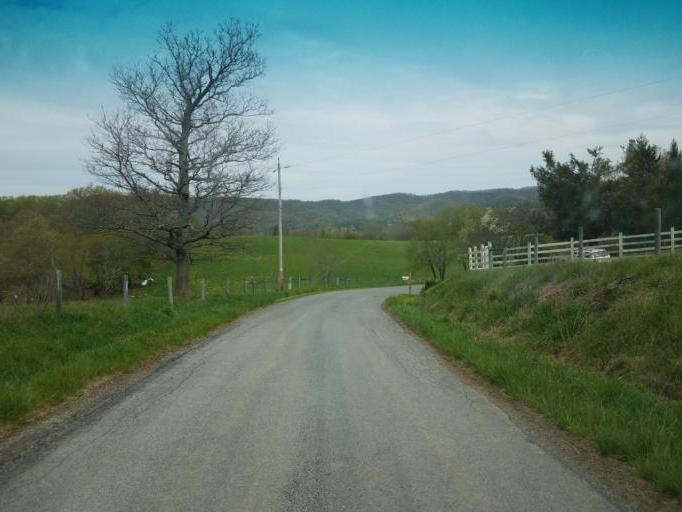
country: US
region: Virginia
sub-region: Smyth County
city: Marion
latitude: 36.7637
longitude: -81.4580
